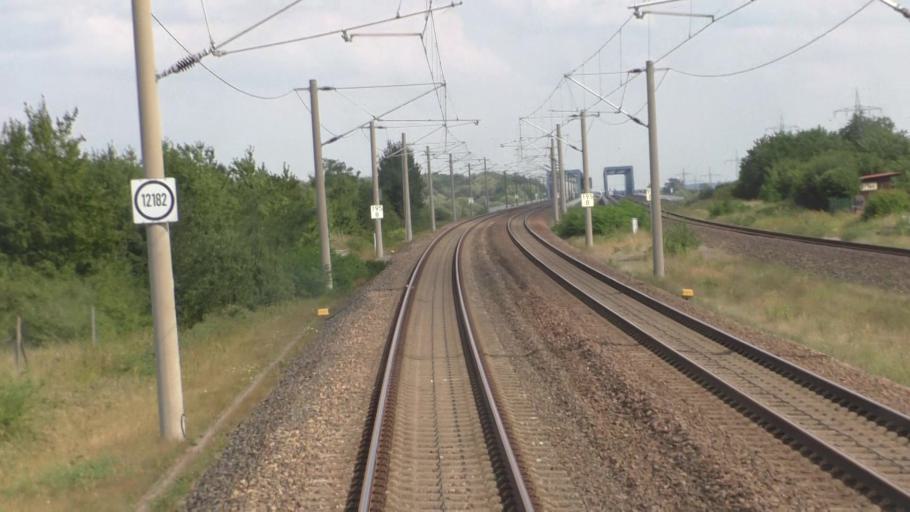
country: DE
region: Saxony-Anhalt
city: Schonhausen
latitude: 52.5999
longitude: 11.9895
